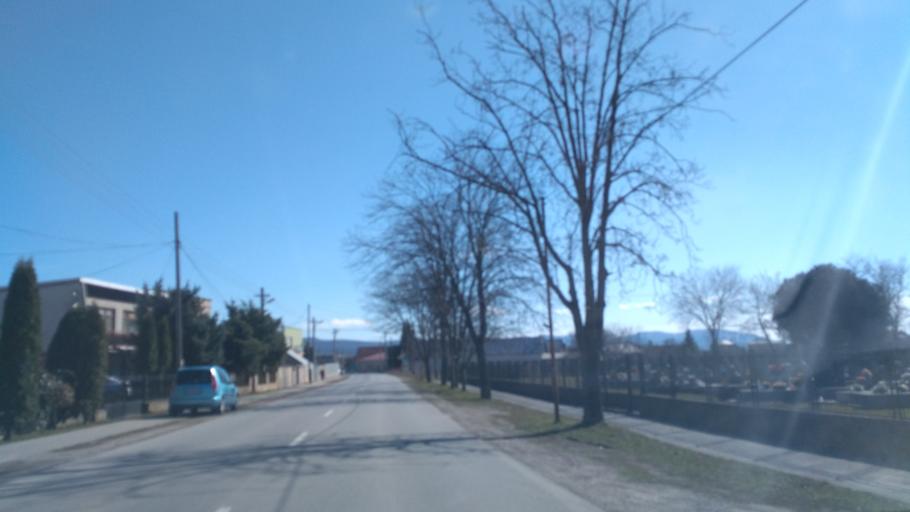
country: SK
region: Kosicky
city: Kosice
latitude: 48.6098
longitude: 21.3207
